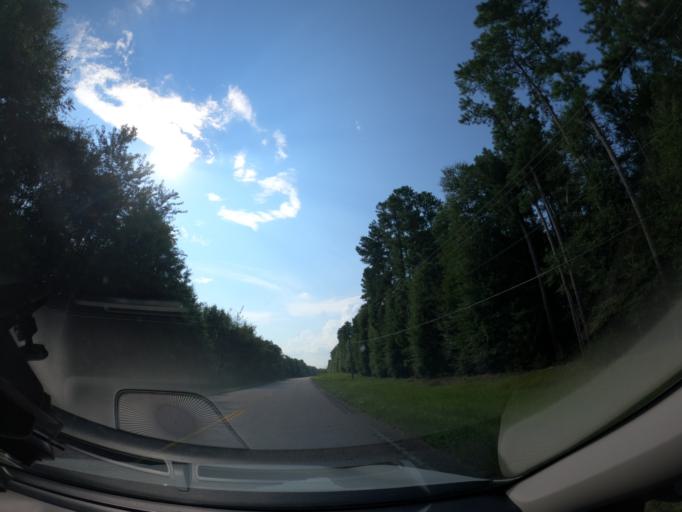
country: US
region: South Carolina
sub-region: Aiken County
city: Clearwater
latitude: 33.4127
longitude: -81.8378
